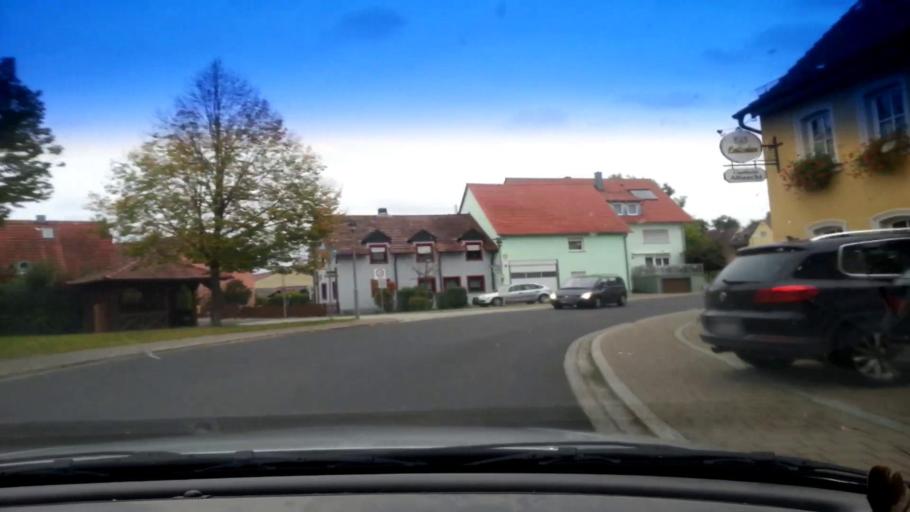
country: DE
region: Bavaria
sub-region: Upper Franconia
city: Lauter
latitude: 49.9725
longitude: 10.7864
